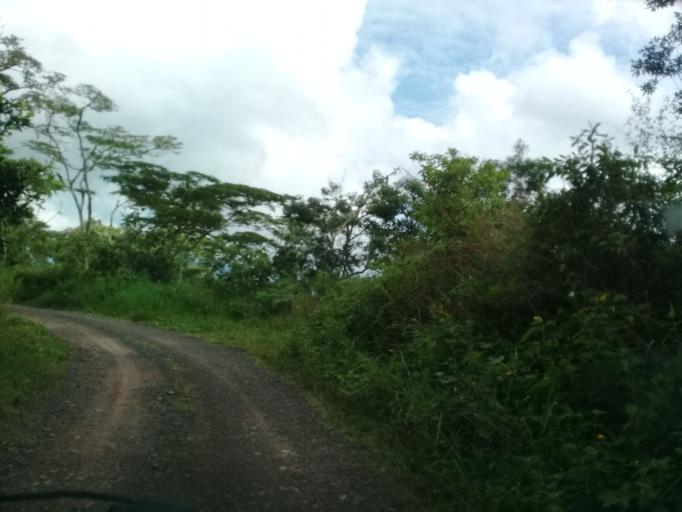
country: CO
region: Cundinamarca
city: Granada
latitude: 5.1045
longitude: -74.5650
